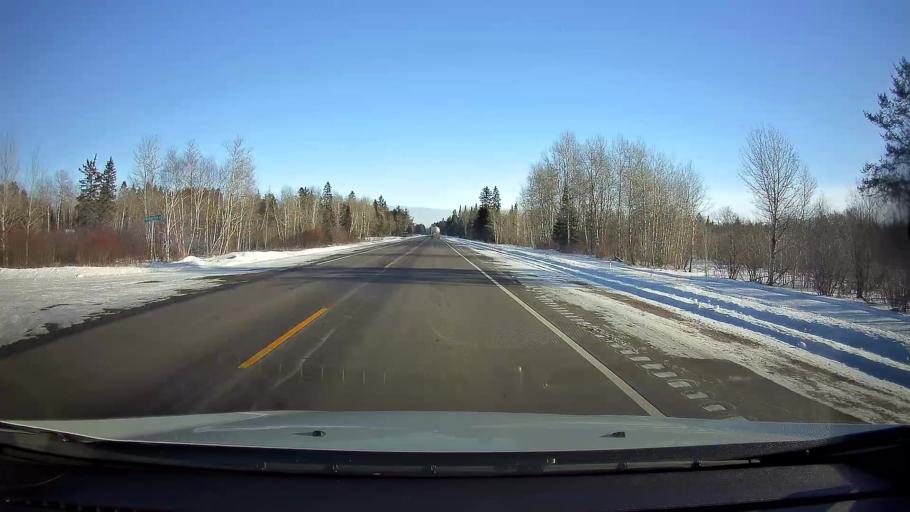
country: US
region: Wisconsin
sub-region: Sawyer County
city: Hayward
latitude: 46.0791
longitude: -91.4045
